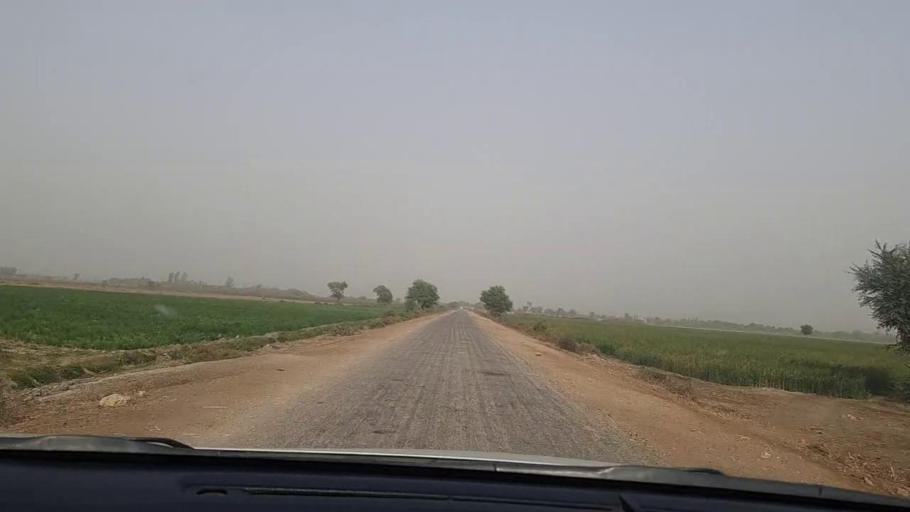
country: PK
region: Sindh
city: Pithoro
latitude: 25.4035
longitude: 69.3876
